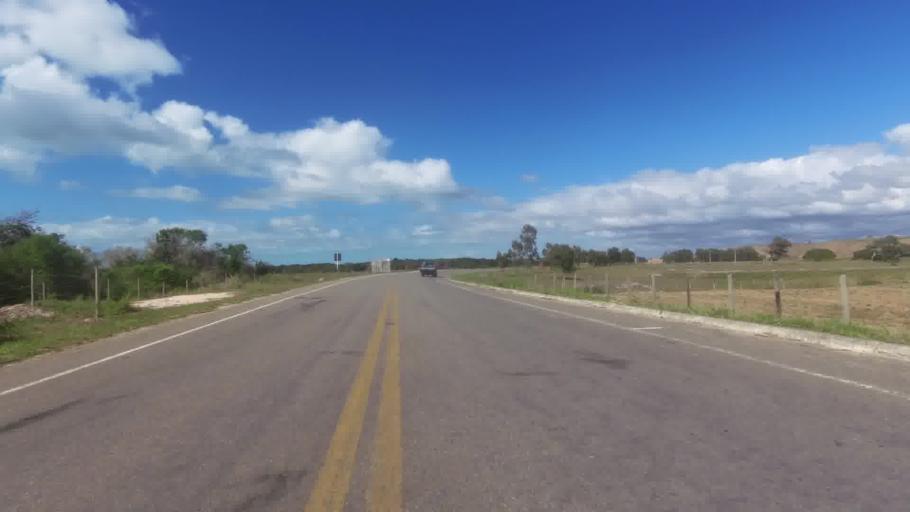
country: BR
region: Espirito Santo
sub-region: Marataizes
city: Marataizes
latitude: -21.1920
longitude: -40.9421
